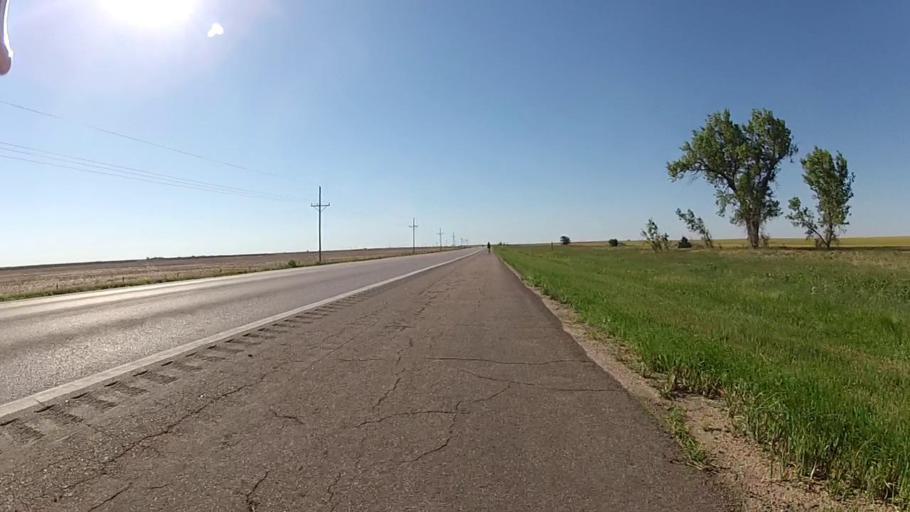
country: US
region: Kansas
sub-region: Ford County
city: Dodge City
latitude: 37.5921
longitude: -99.6905
